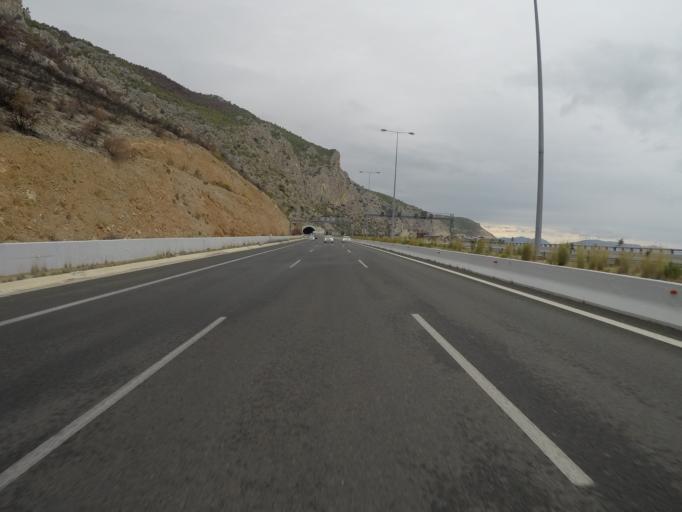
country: GR
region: Attica
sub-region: Nomarchia Dytikis Attikis
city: Kineta
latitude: 37.9782
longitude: 23.2612
